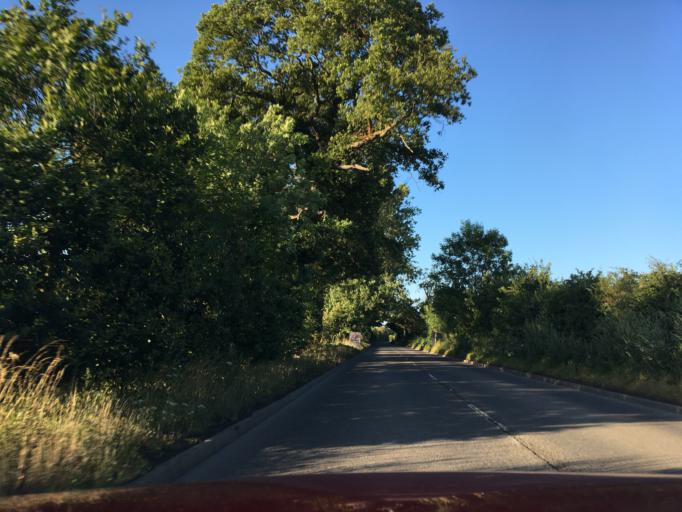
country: GB
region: England
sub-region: Hampshire
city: Tadley
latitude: 51.3939
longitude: -1.1455
